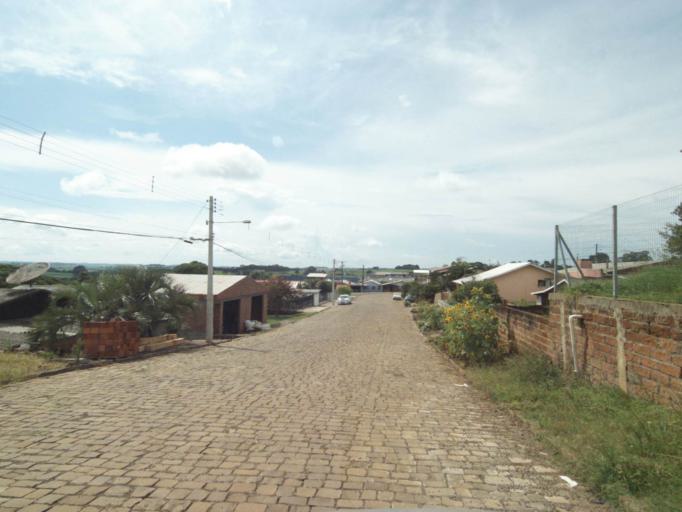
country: BR
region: Rio Grande do Sul
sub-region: Lagoa Vermelha
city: Lagoa Vermelha
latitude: -28.2229
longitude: -51.5119
